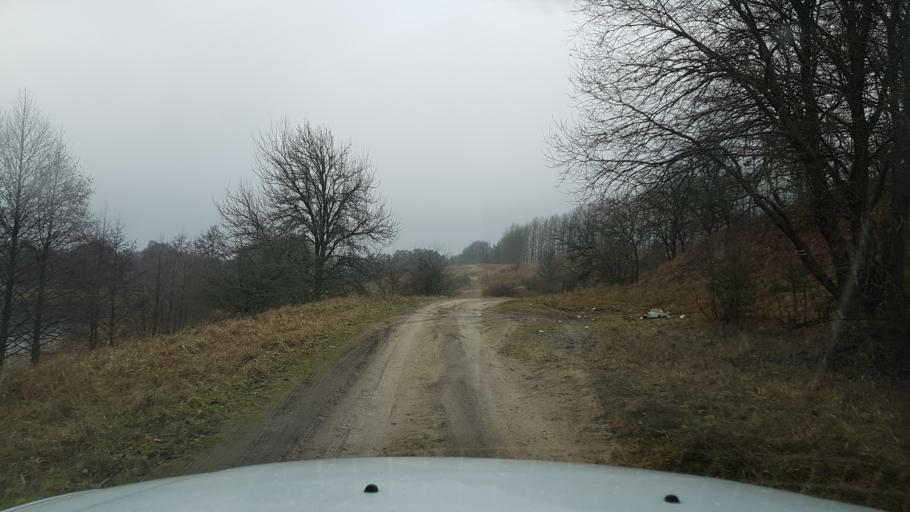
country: PL
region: West Pomeranian Voivodeship
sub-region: Powiat drawski
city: Czaplinek
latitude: 53.5649
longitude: 16.2471
